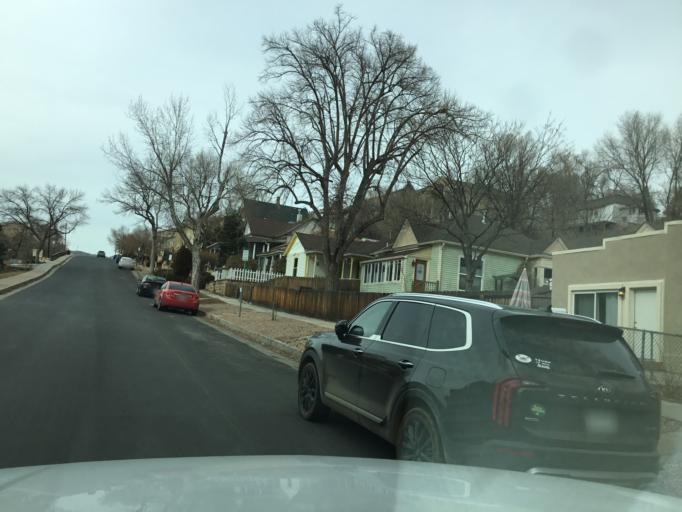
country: US
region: Colorado
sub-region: El Paso County
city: Colorado Springs
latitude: 38.8480
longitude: -104.8620
